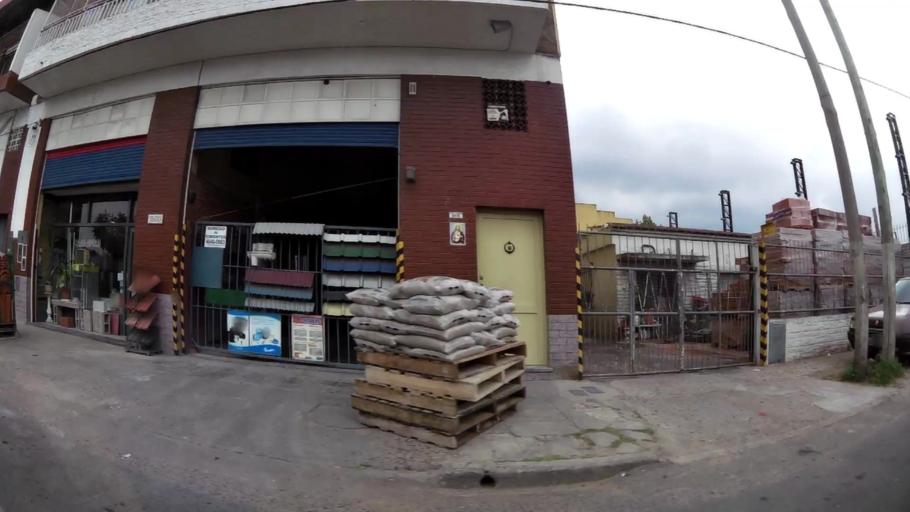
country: AR
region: Buenos Aires
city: San Justo
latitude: -34.7101
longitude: -58.5276
